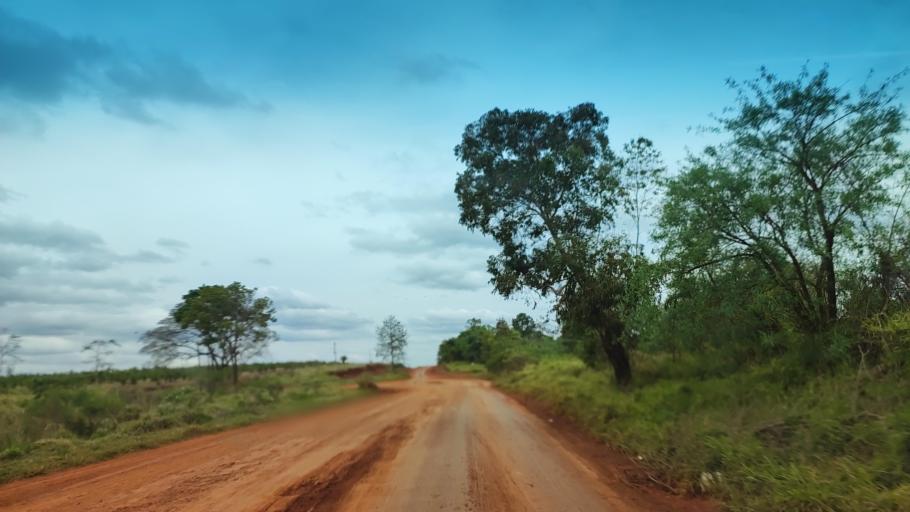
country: AR
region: Misiones
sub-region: Departamento de Capital
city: Posadas
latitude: -27.4832
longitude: -55.9708
